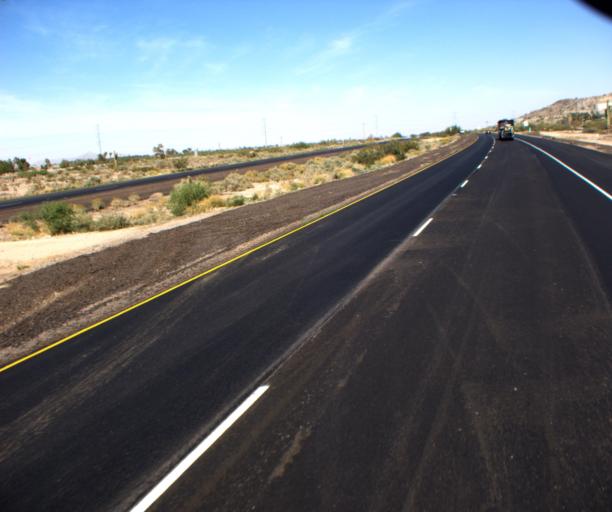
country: US
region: Arizona
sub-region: Pinal County
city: Casa Grande
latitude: 32.8298
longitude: -111.7347
